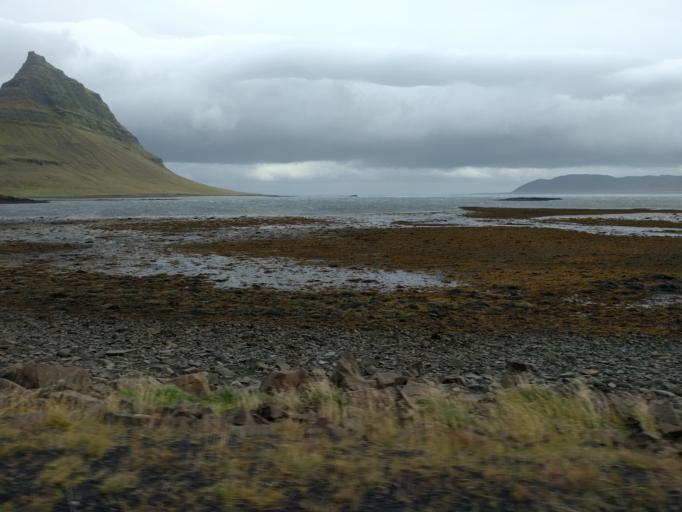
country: IS
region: West
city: Olafsvik
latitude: 64.9222
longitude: -23.2911
